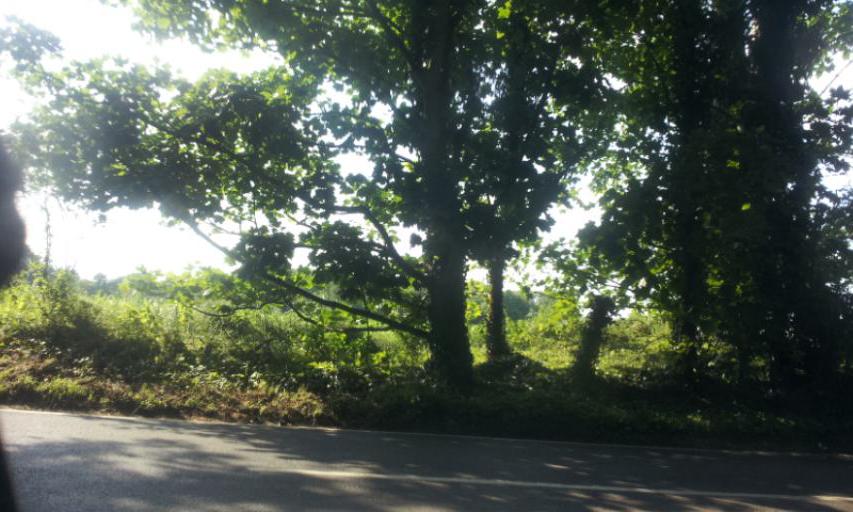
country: GB
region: England
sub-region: Kent
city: Harrietsham
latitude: 51.2629
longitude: 0.6390
